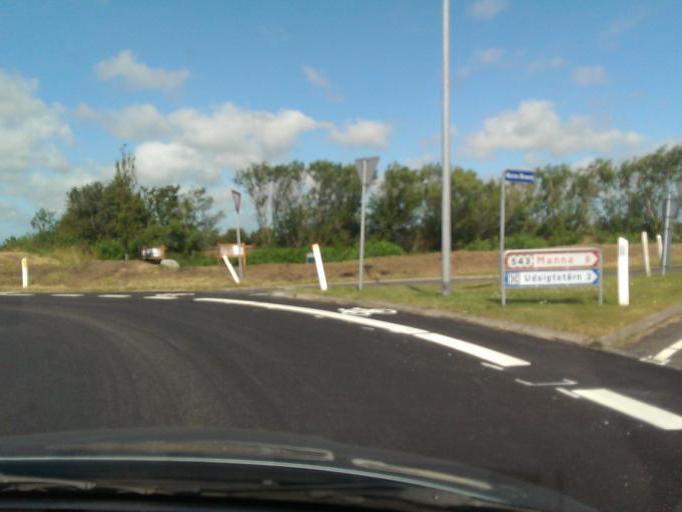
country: DK
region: North Denmark
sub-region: Alborg Kommune
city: Vadum
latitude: 57.2169
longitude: 9.8378
